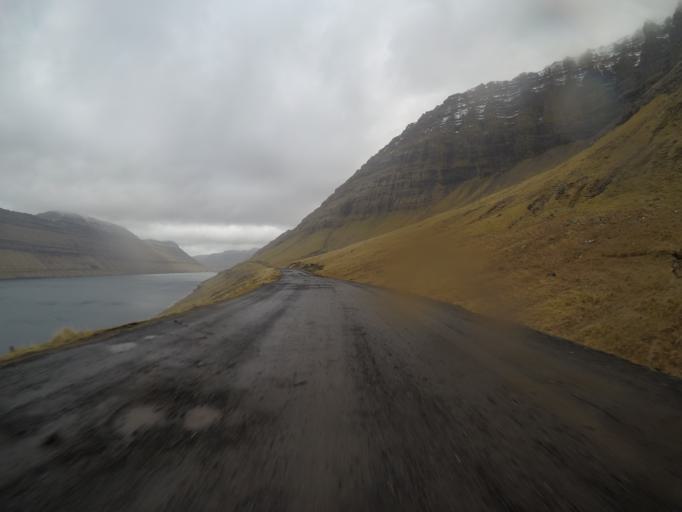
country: FO
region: Nordoyar
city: Klaksvik
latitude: 62.3361
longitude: -6.5780
